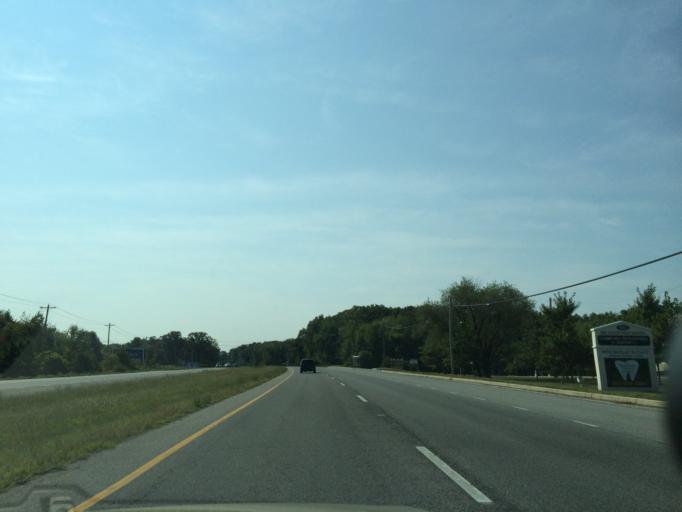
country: US
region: Maryland
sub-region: Charles County
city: La Plata
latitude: 38.4527
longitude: -76.9907
